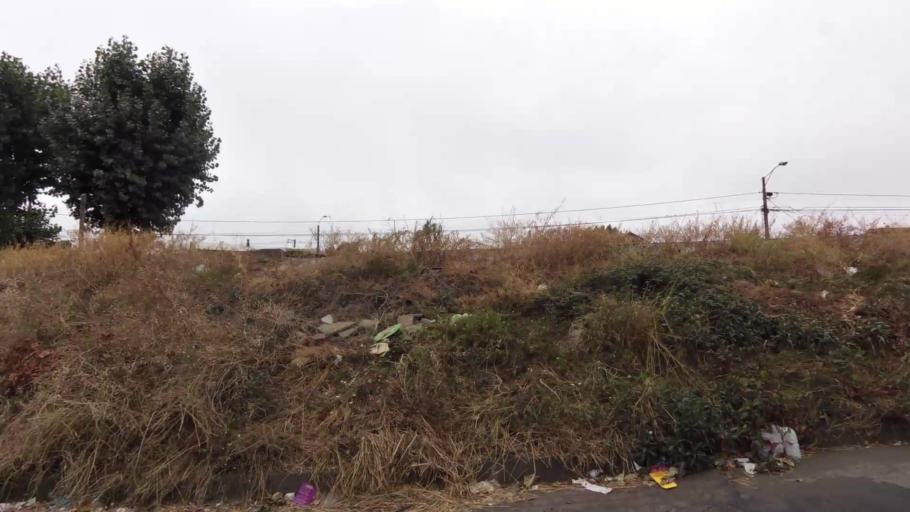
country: CL
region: Biobio
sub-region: Provincia de Concepcion
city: Concepcion
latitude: -36.8101
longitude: -73.0426
